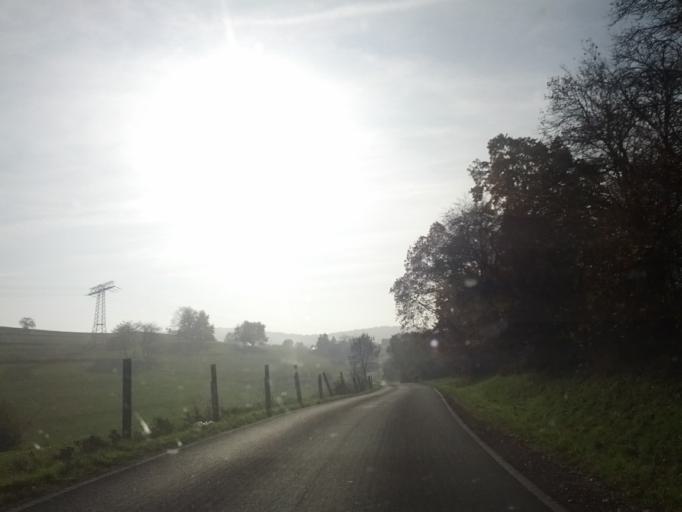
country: DE
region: Thuringia
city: Thal
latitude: 50.9316
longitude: 10.3909
